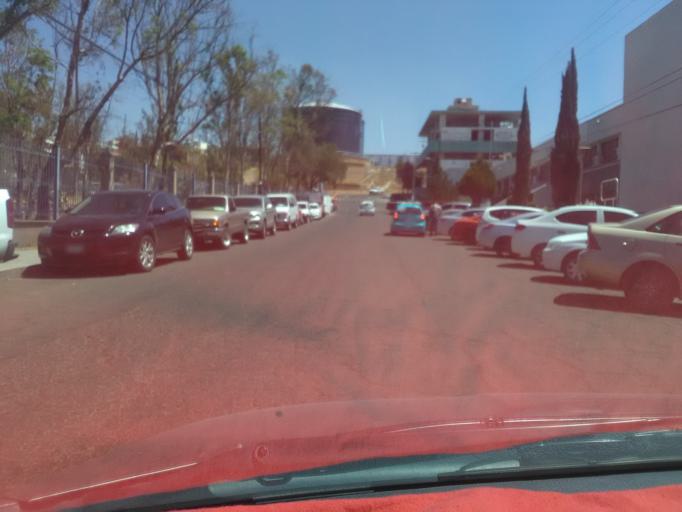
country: MX
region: Durango
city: Victoria de Durango
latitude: 24.0154
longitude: -104.6821
